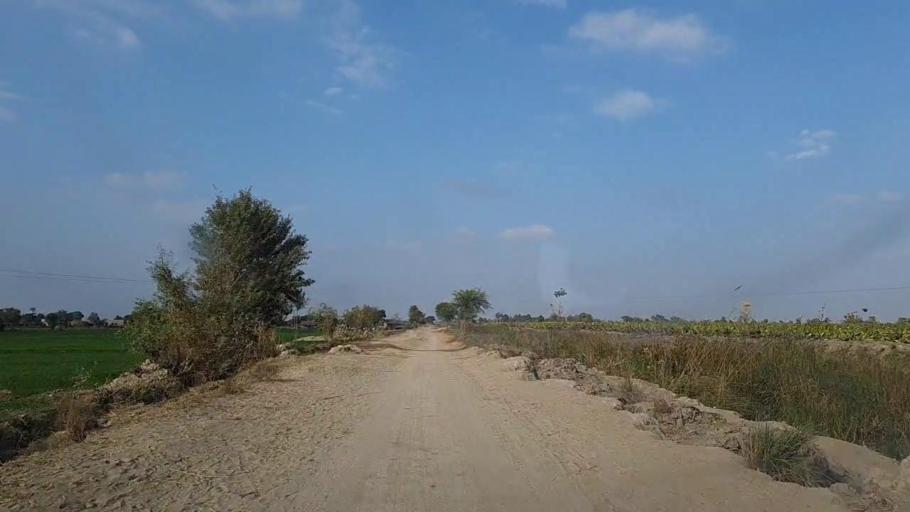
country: PK
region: Sindh
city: Sanghar
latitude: 26.2361
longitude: 68.9729
